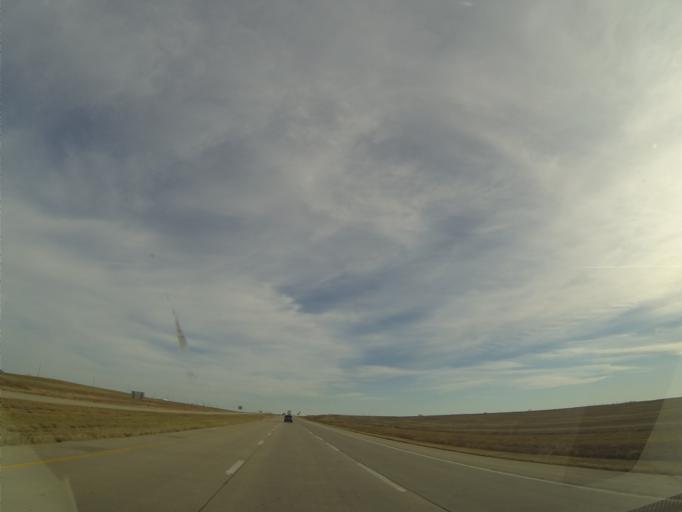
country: US
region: Kansas
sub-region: Ottawa County
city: Minneapolis
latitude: 39.1130
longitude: -97.6626
